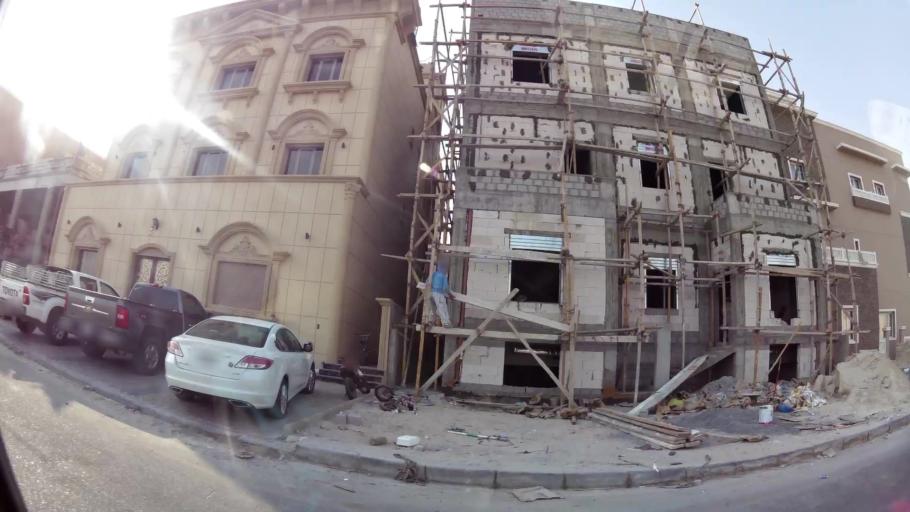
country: KW
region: Al Asimah
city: Ar Rabiyah
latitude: 29.3274
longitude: 47.8115
